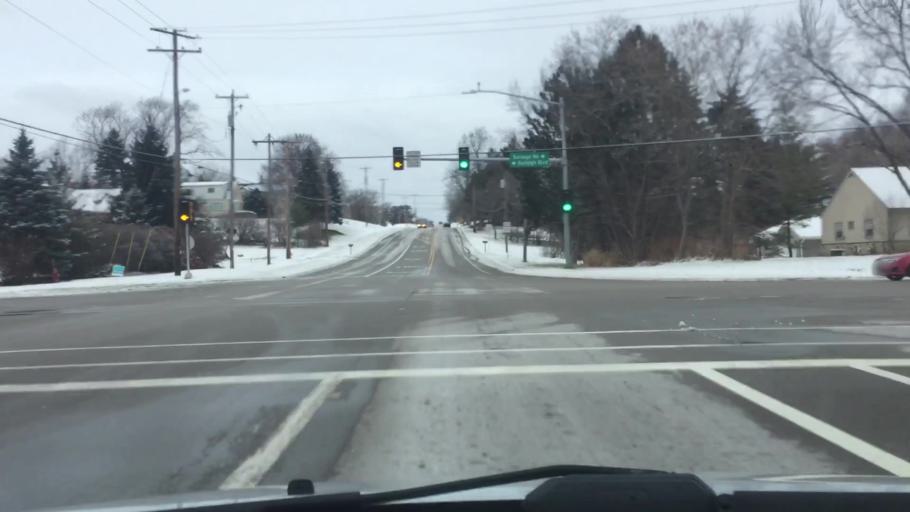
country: US
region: Wisconsin
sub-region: Waukesha County
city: Brookfield
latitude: 43.0749
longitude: -88.1059
